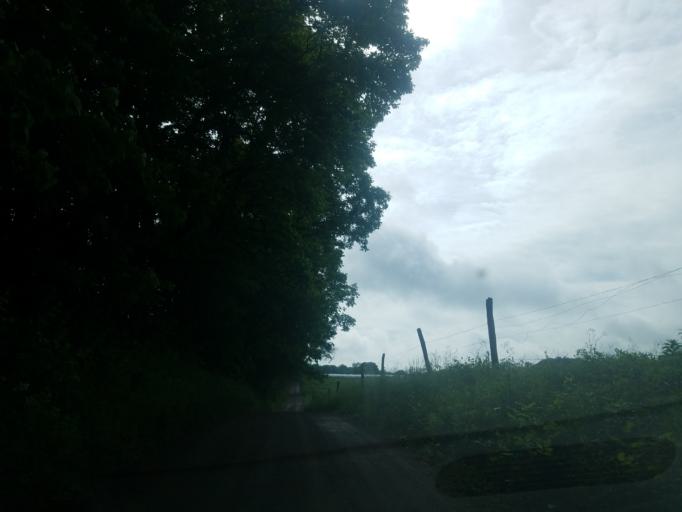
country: US
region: Ohio
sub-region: Holmes County
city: Millersburg
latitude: 40.5139
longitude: -81.8610
